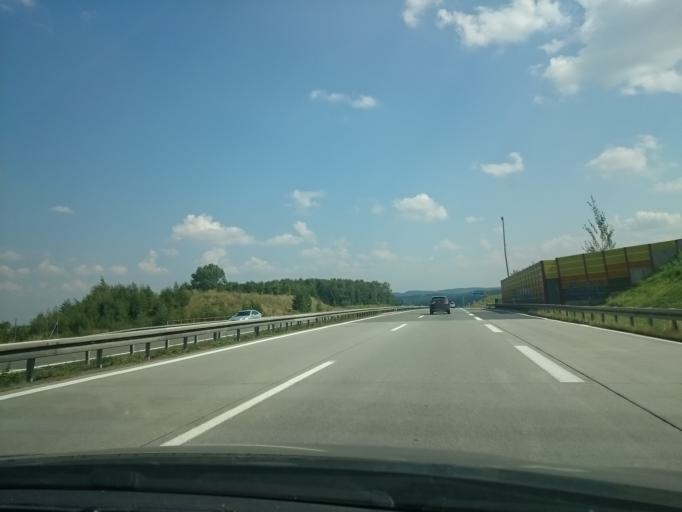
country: DE
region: Saxony
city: Oelsnitz
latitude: 50.6916
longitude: 12.6980
